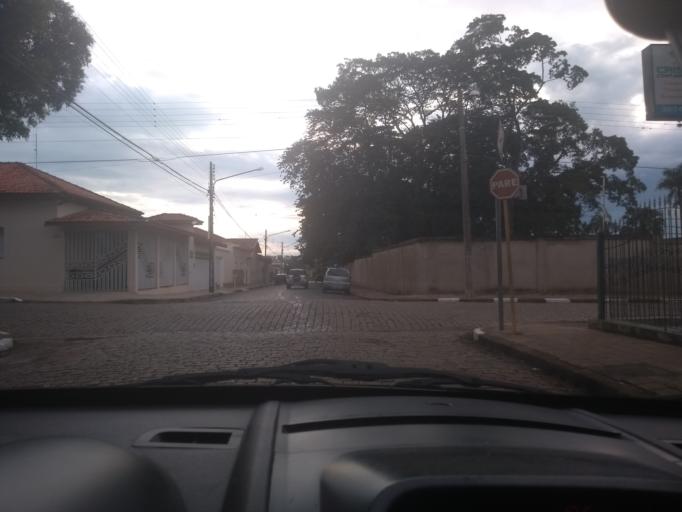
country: BR
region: Sao Paulo
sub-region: Casa Branca
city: Casa Branca
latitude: -21.7768
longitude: -47.0827
